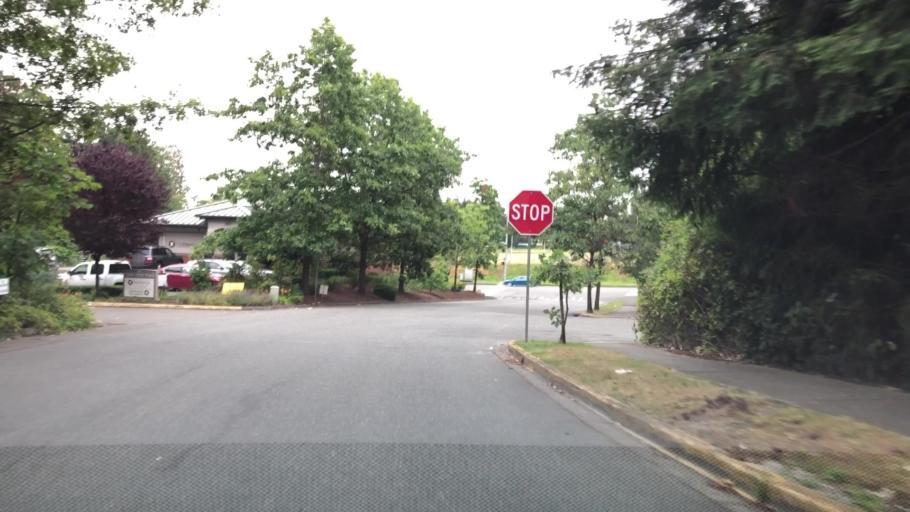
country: US
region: Washington
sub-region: Snohomish County
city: Alderwood Manor
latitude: 47.8197
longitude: -122.2745
